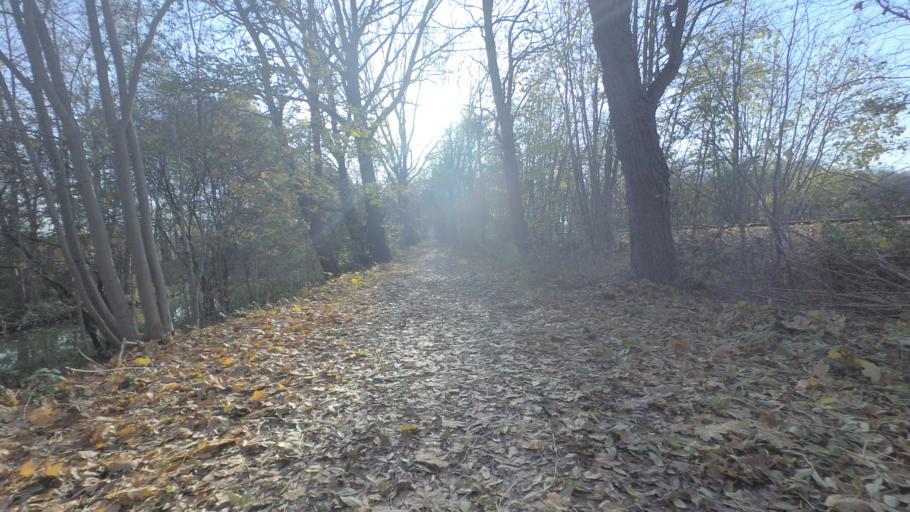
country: DE
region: Brandenburg
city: Am Mellensee
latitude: 52.2011
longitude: 13.4168
